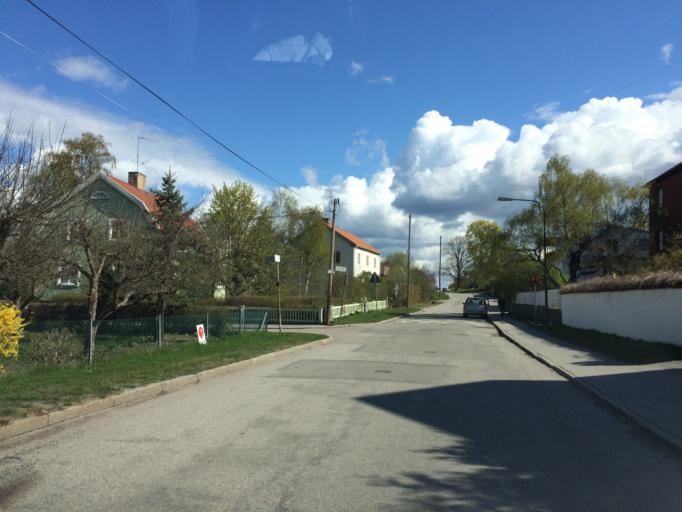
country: SE
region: Stockholm
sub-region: Huddinge Kommun
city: Segeltorp
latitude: 59.2993
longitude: 17.9497
